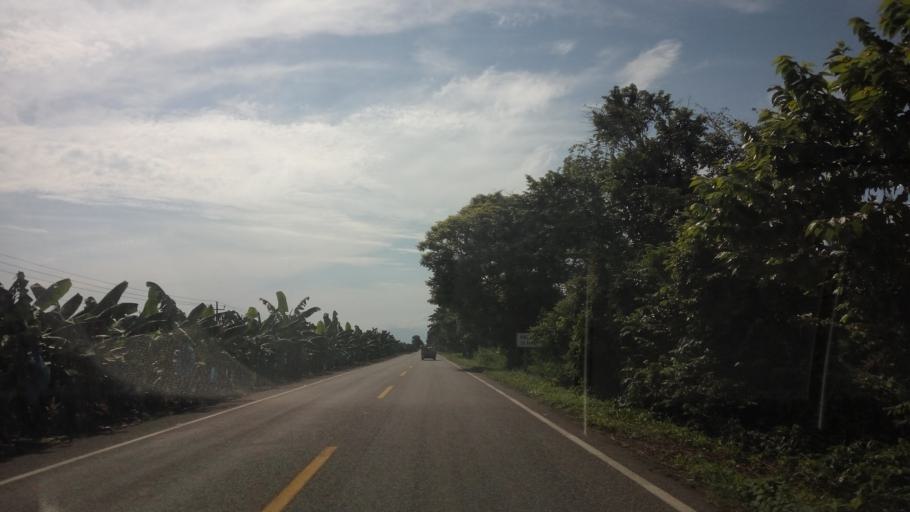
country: MX
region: Tabasco
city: Rio de Teapa
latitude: 17.7025
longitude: -92.9503
